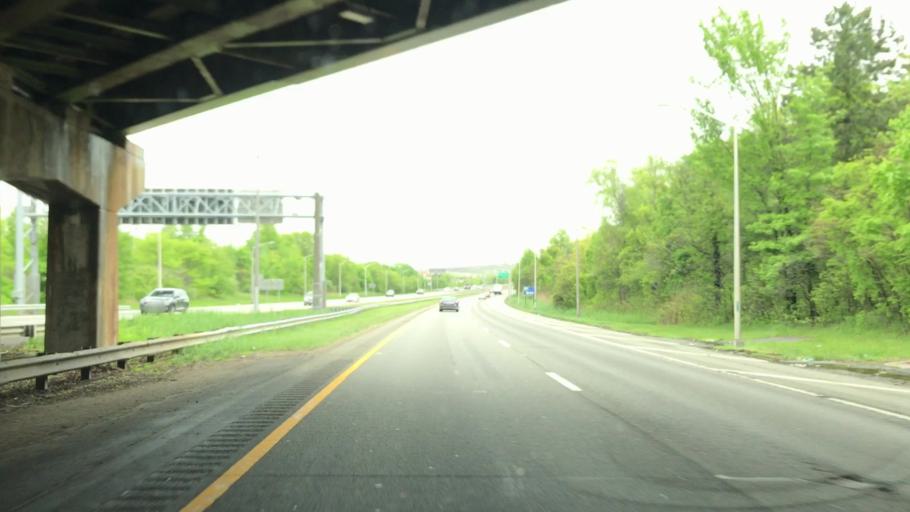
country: US
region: New Jersey
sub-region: Middlesex County
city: Carteret
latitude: 40.5484
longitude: -74.2205
